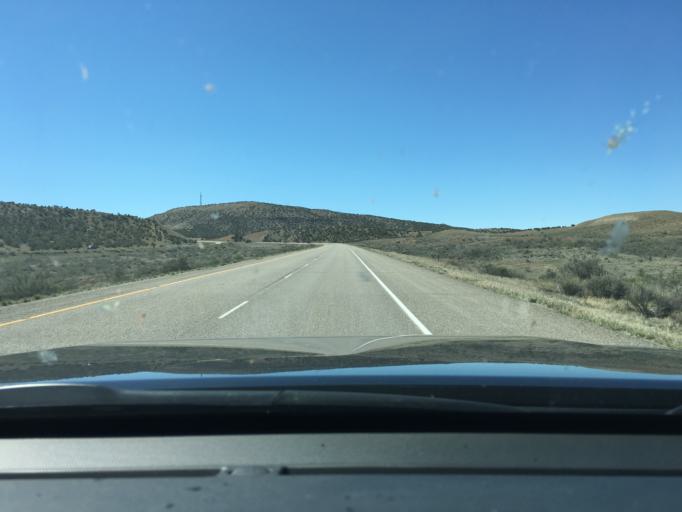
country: US
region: Colorado
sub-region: Mesa County
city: Loma
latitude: 39.2227
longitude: -108.9501
